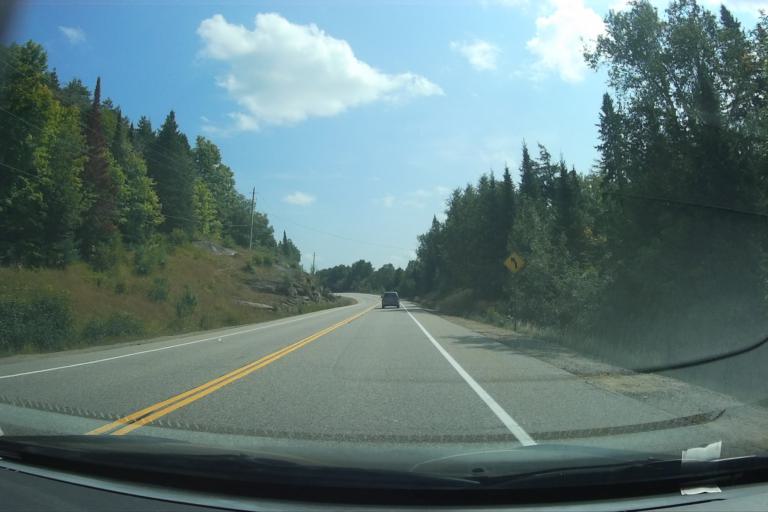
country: CA
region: Ontario
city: Mattawa
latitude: 45.5847
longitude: -78.4762
